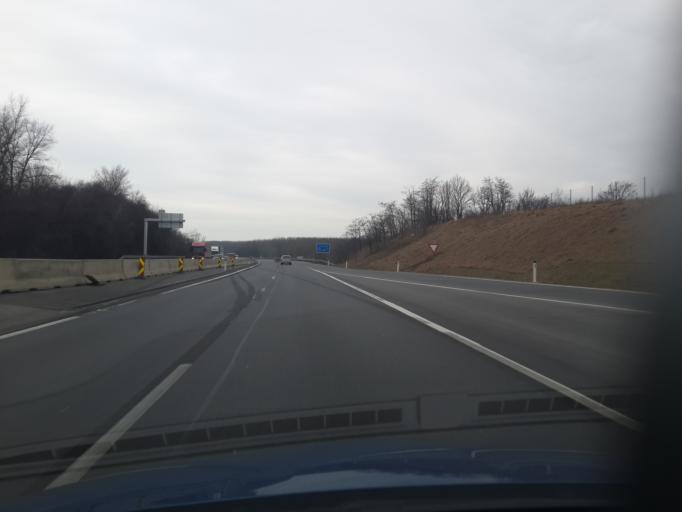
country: AT
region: Lower Austria
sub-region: Politischer Bezirk Wien-Umgebung
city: Fischamend Dorf
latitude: 48.1177
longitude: 16.6271
